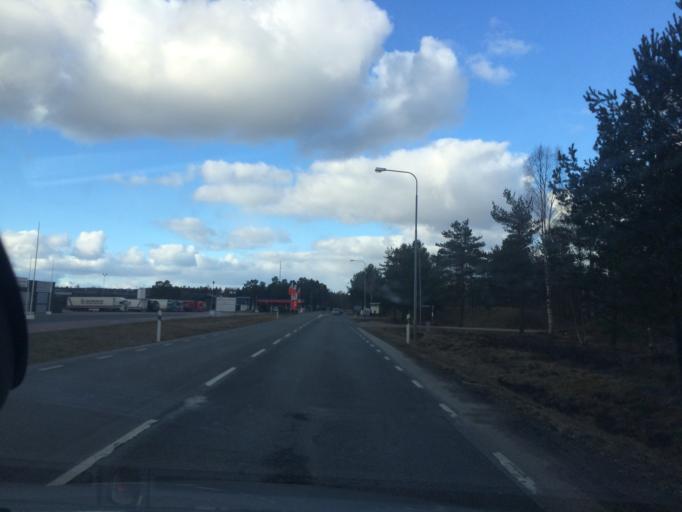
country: SE
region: Joenkoeping
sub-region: Vaggeryds Kommun
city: Skillingaryd
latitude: 57.3474
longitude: 14.0994
